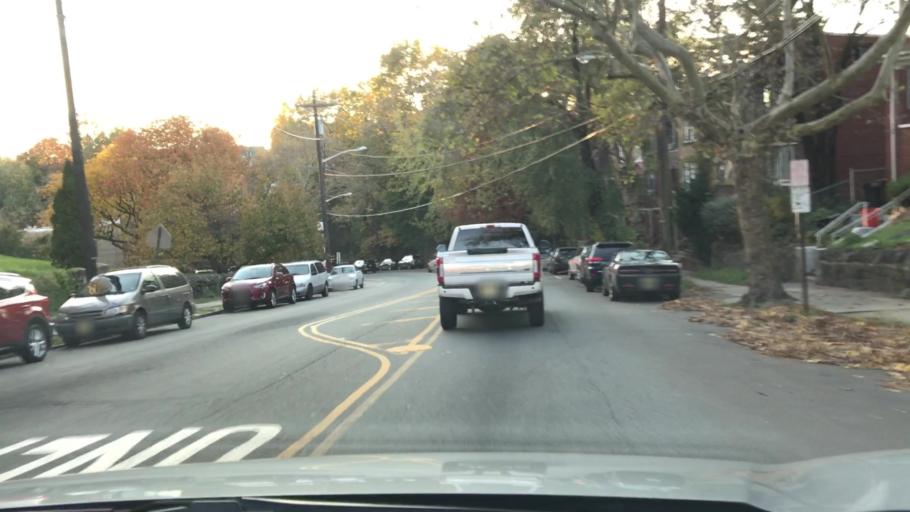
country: US
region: New Jersey
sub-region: Hudson County
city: Weehawken
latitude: 40.7712
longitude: -74.0196
